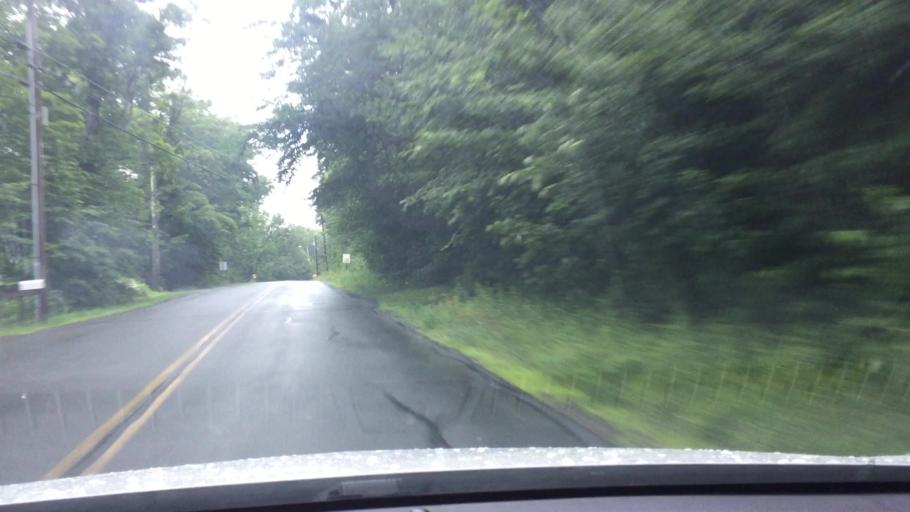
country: US
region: Massachusetts
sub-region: Berkshire County
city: Becket
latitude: 42.2909
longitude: -73.0567
